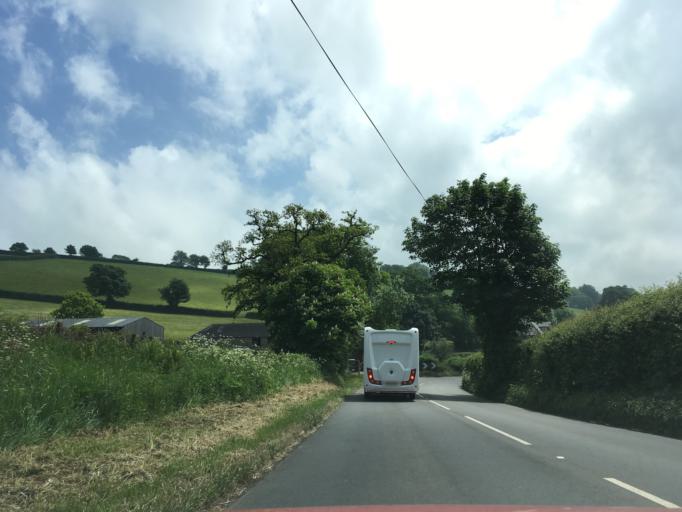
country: GB
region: England
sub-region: Devon
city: Totnes
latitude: 50.4028
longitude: -3.7118
